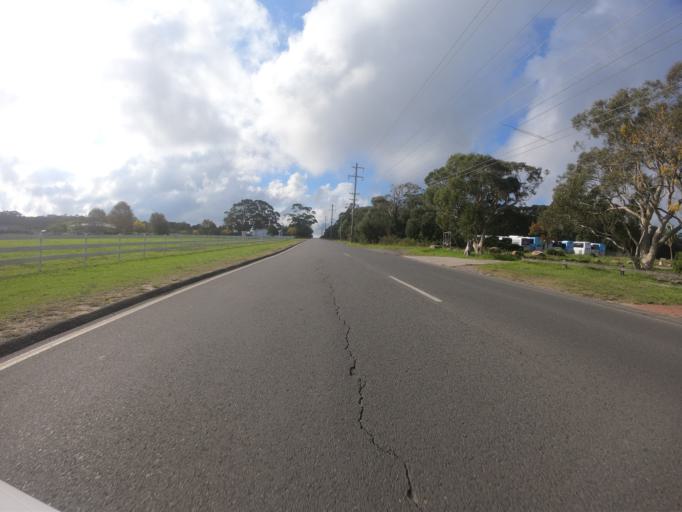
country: AU
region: New South Wales
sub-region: Wollongong
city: Helensburgh
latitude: -34.2046
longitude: 150.9793
